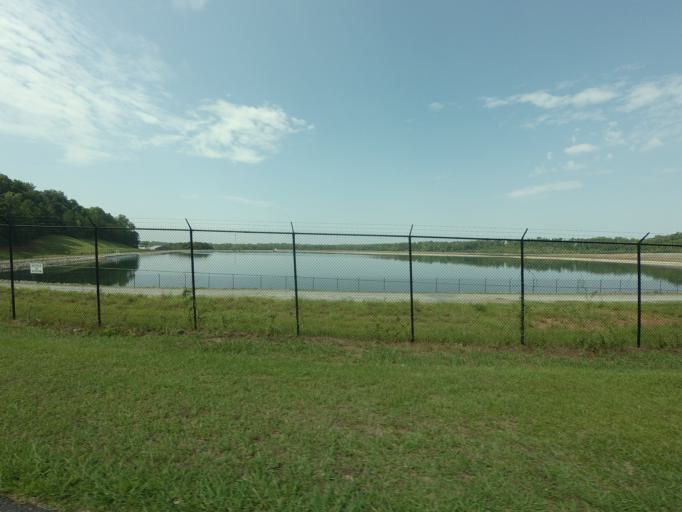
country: US
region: Georgia
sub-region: Fulton County
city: Johns Creek
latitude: 34.0226
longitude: -84.2231
